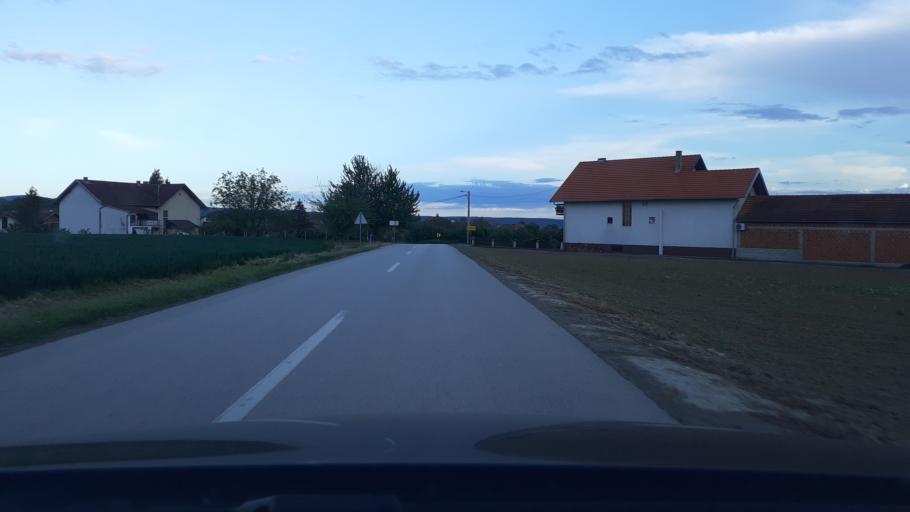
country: HR
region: Pozesko-Slavonska
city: Jaksic
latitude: 45.3409
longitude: 17.7929
